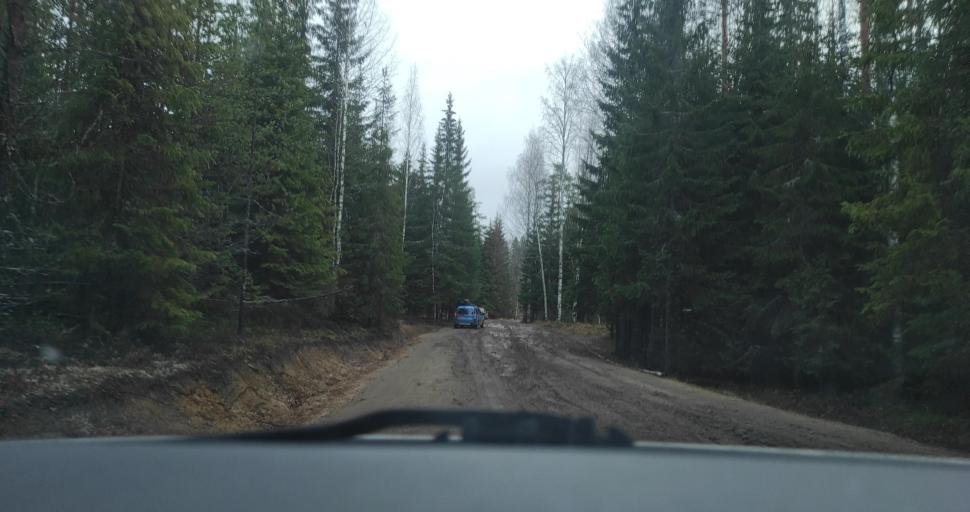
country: RU
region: Republic of Karelia
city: Pitkyaranta
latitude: 61.7527
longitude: 31.4040
